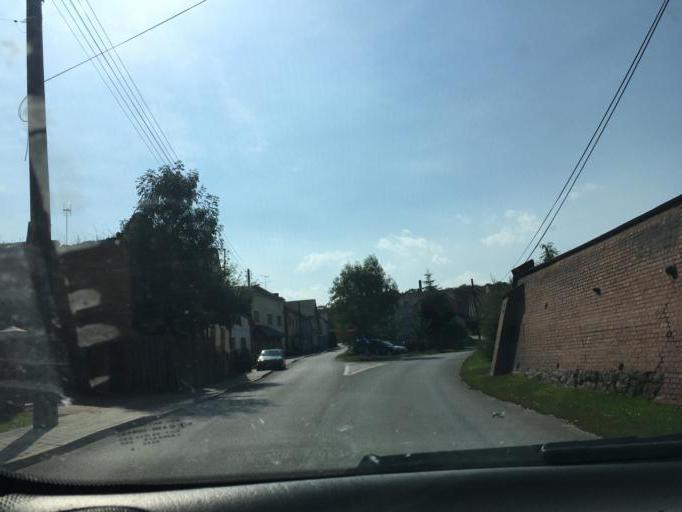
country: PL
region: Opole Voivodeship
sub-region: Powiat prudnicki
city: Raclawice Slaskie
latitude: 50.3037
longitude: 17.8117
